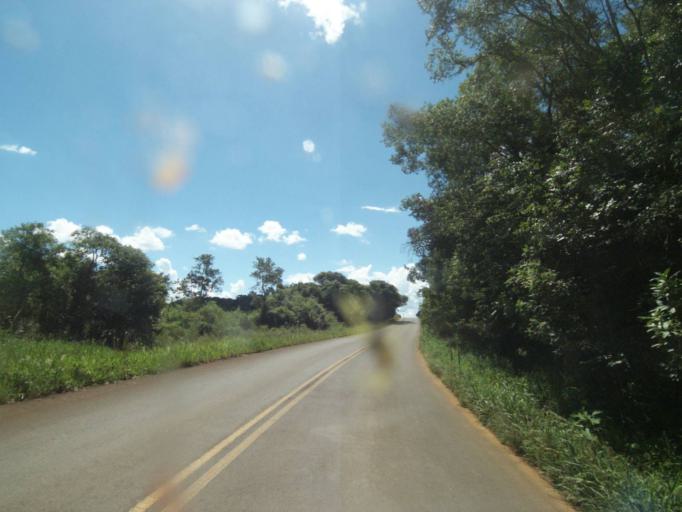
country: BR
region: Parana
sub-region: Pinhao
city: Pinhao
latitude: -25.7947
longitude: -52.0774
